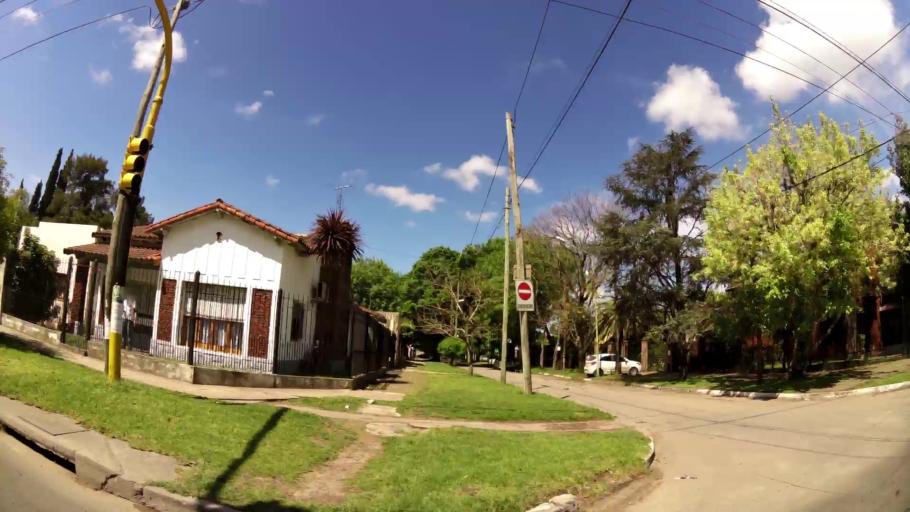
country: AR
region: Buenos Aires
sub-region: Partido de Quilmes
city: Quilmes
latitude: -34.8138
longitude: -58.2726
